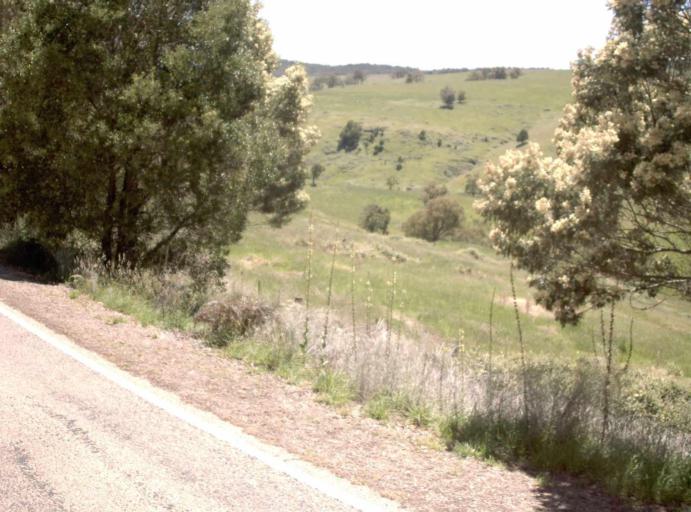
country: AU
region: Victoria
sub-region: East Gippsland
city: Lakes Entrance
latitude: -37.2454
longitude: 148.2552
